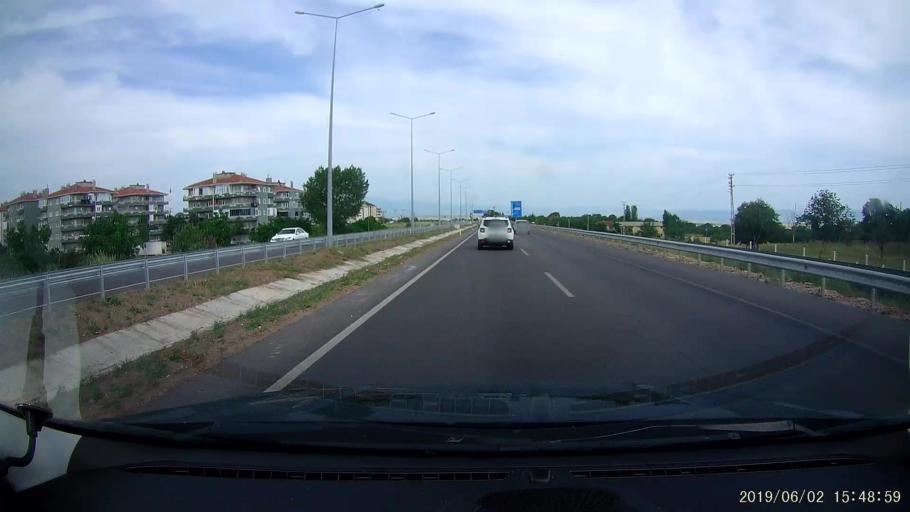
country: TR
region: Amasya
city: Merzifon
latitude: 40.8594
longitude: 35.4528
